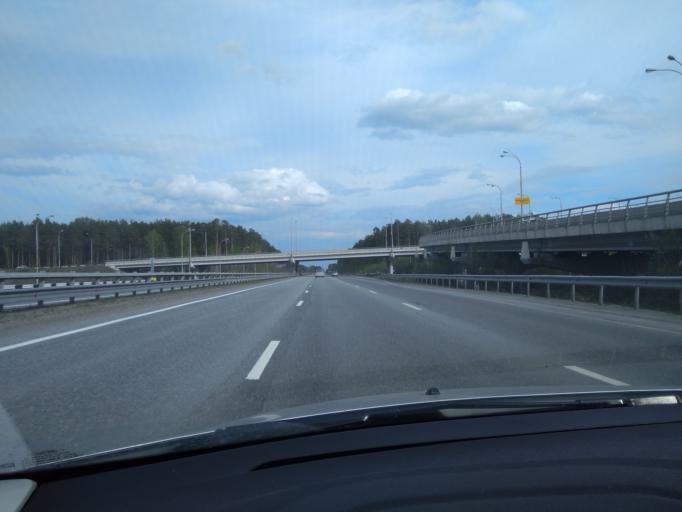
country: RU
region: Sverdlovsk
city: Shuvakish
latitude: 56.8941
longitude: 60.5322
